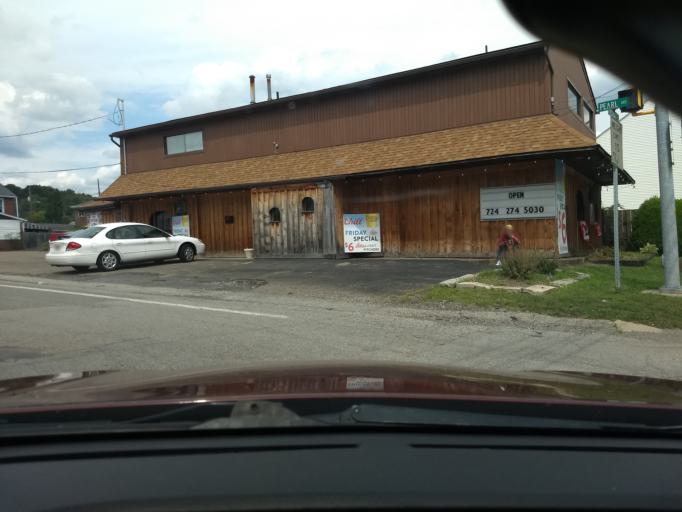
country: US
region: Pennsylvania
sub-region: Allegheny County
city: Cheswick
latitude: 40.5408
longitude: -79.8162
